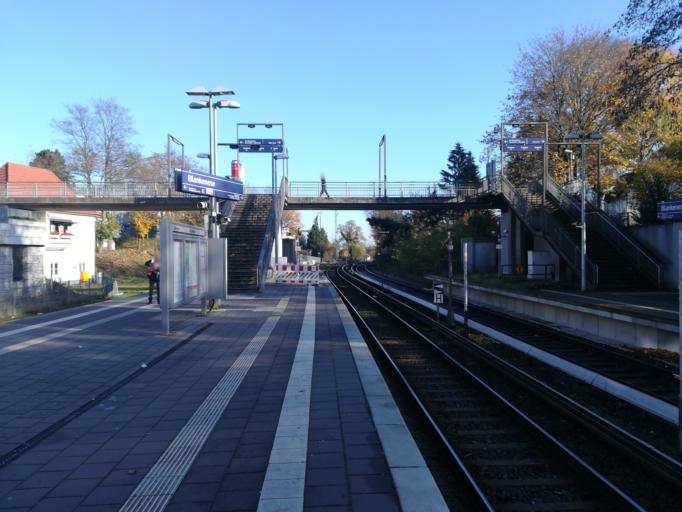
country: DE
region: Schleswig-Holstein
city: Halstenbek
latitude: 53.5647
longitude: 9.8161
